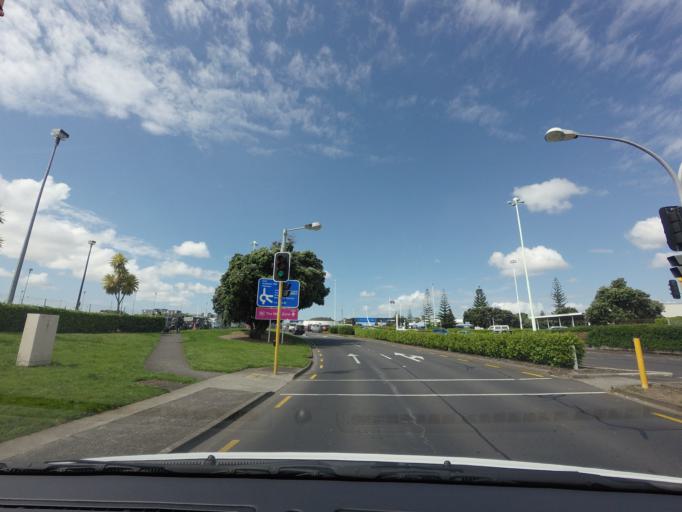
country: NZ
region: Auckland
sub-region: Auckland
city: Mangere
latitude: -37.0028
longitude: 174.7852
